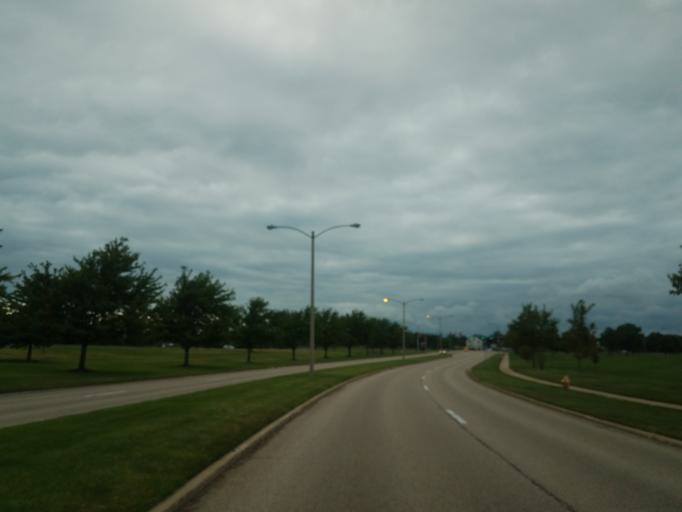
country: US
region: Illinois
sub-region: McLean County
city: Bloomington
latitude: 40.4611
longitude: -88.9547
